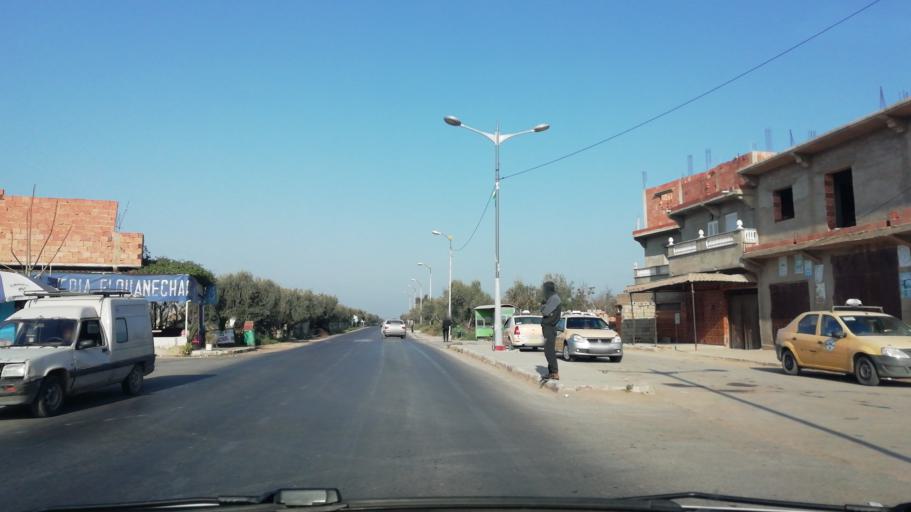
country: DZ
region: Mostaganem
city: Mostaganem
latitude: 35.7534
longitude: 0.1174
